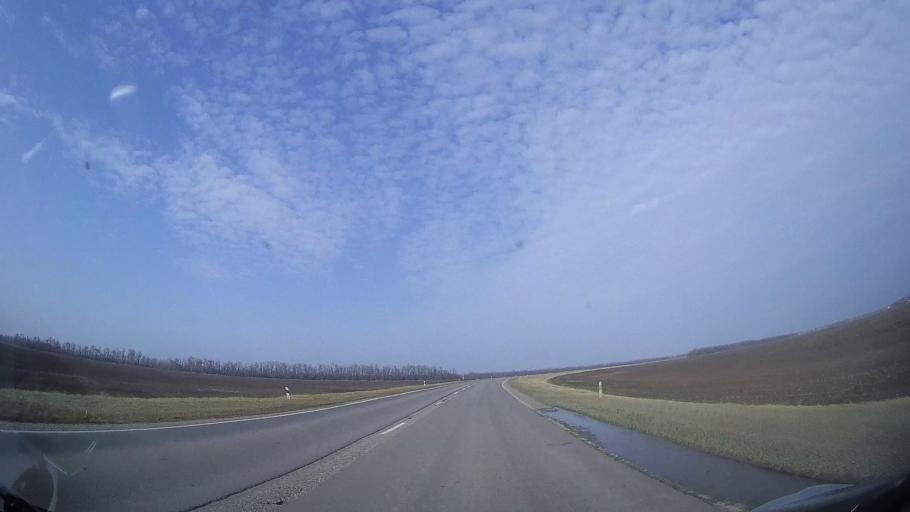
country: RU
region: Rostov
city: Tselina
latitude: 46.5128
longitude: 41.0017
